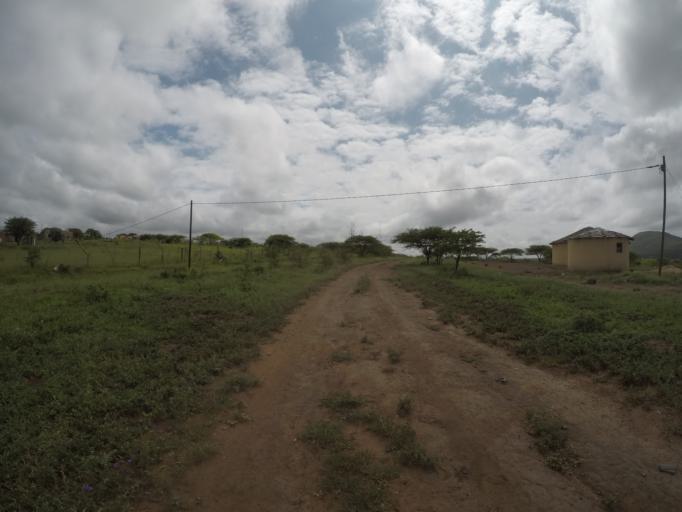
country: ZA
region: KwaZulu-Natal
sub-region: uThungulu District Municipality
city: Empangeni
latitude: -28.5841
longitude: 31.8528
